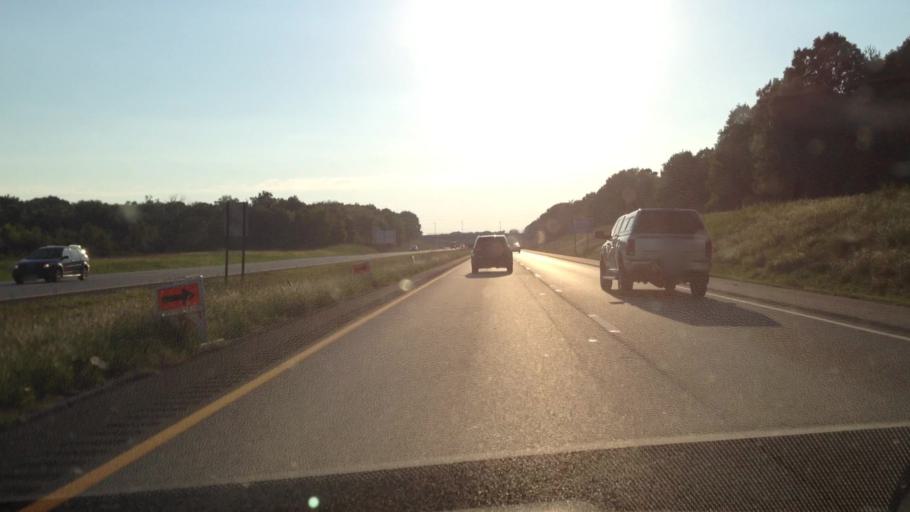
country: US
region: Missouri
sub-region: Jasper County
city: Duquesne
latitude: 37.0461
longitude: -94.4897
